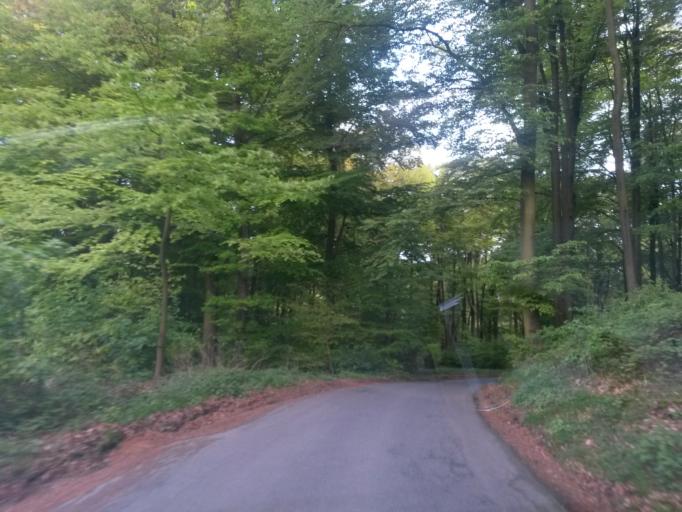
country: DE
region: North Rhine-Westphalia
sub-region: Regierungsbezirk Arnsberg
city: Nachrodt-Wiblingwerde
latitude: 51.3100
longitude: 7.5594
